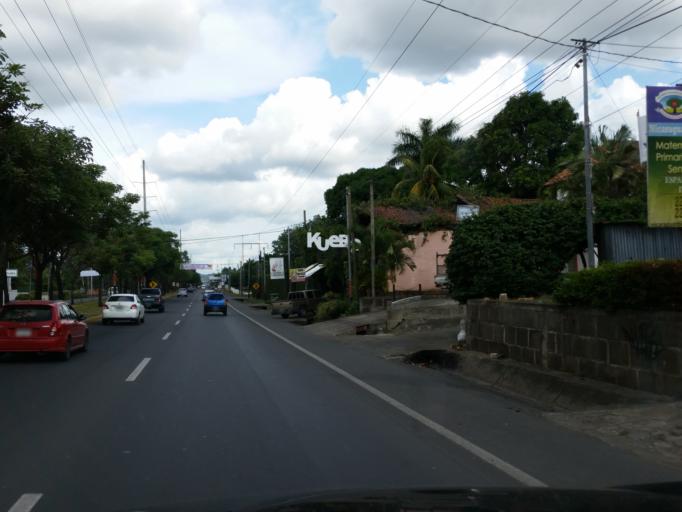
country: NI
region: Managua
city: Managua
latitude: 12.0806
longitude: -86.2256
